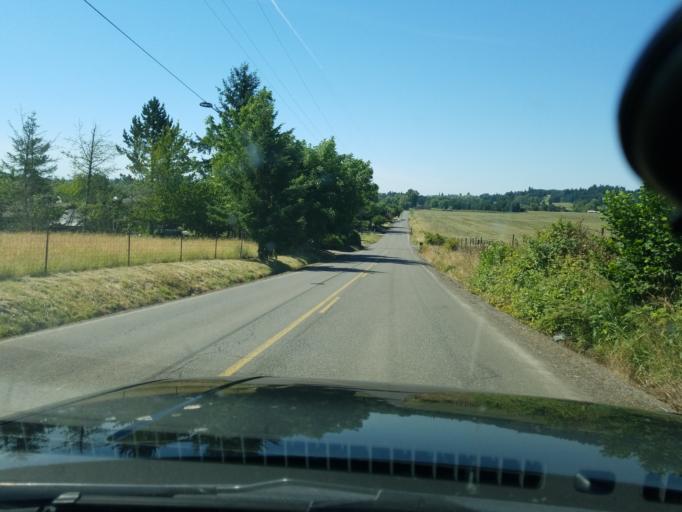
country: US
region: Oregon
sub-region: Yamhill County
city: McMinnville
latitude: 45.2389
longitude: -123.2309
